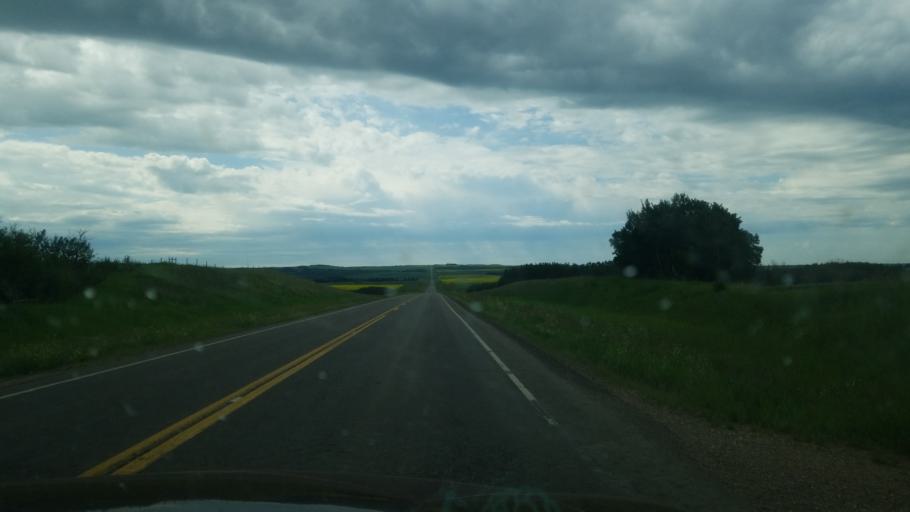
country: CA
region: Saskatchewan
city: Unity
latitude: 52.9221
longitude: -109.3425
